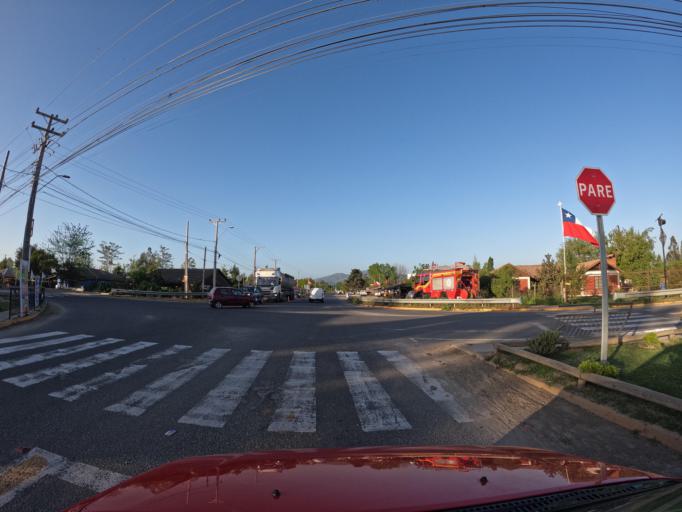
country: CL
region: O'Higgins
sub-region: Provincia de Cachapoal
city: San Vicente
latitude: -34.3118
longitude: -71.3840
